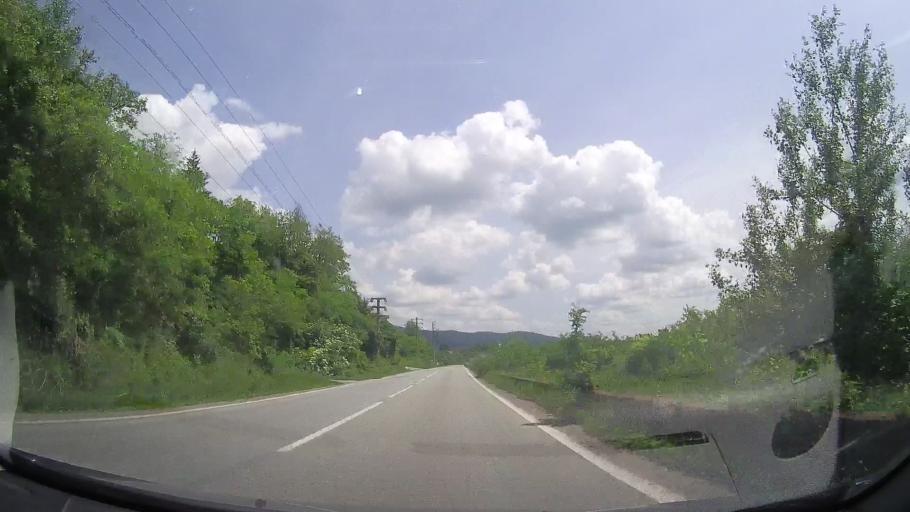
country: RO
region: Valcea
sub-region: Oras Calimanesti
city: Jiblea Veche
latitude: 45.2475
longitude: 24.3442
